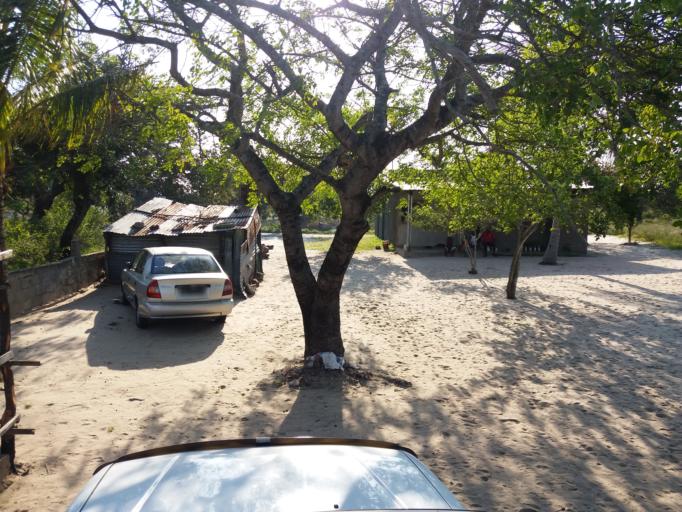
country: MZ
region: Maputo City
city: Maputo
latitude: -25.7592
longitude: 32.6067
